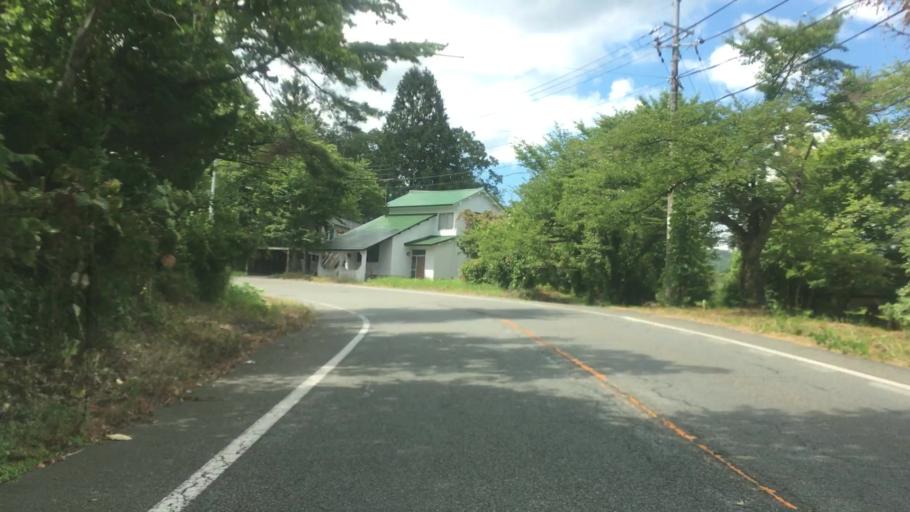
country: JP
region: Hyogo
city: Toyooka
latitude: 35.4923
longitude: 134.6892
